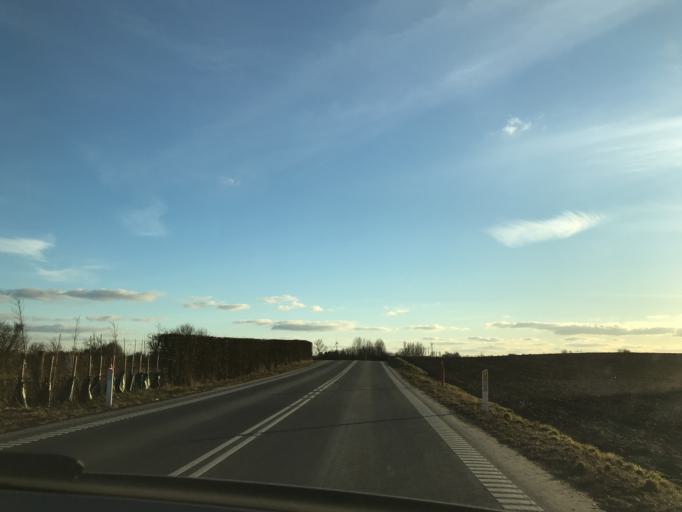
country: DK
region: South Denmark
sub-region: Middelfart Kommune
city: Brenderup
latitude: 55.4746
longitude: 9.9695
